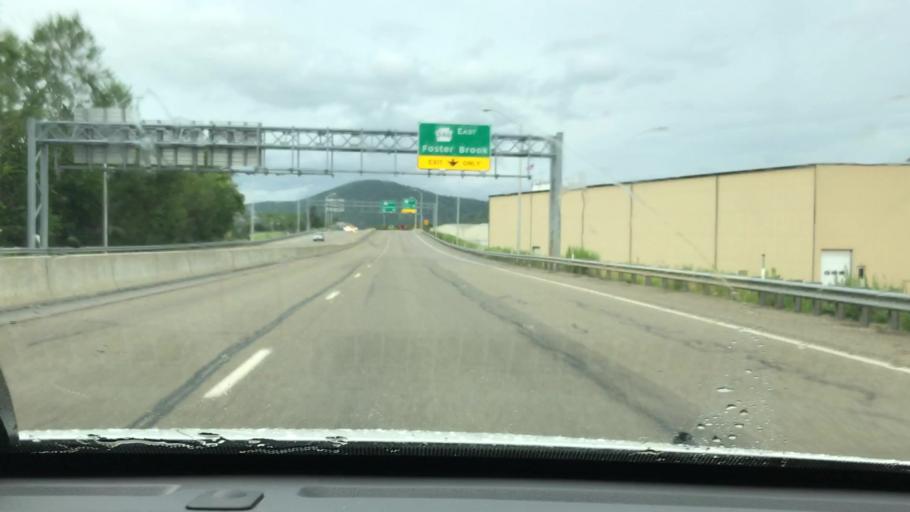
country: US
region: Pennsylvania
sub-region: McKean County
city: Foster Brook
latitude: 41.9735
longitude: -78.6272
